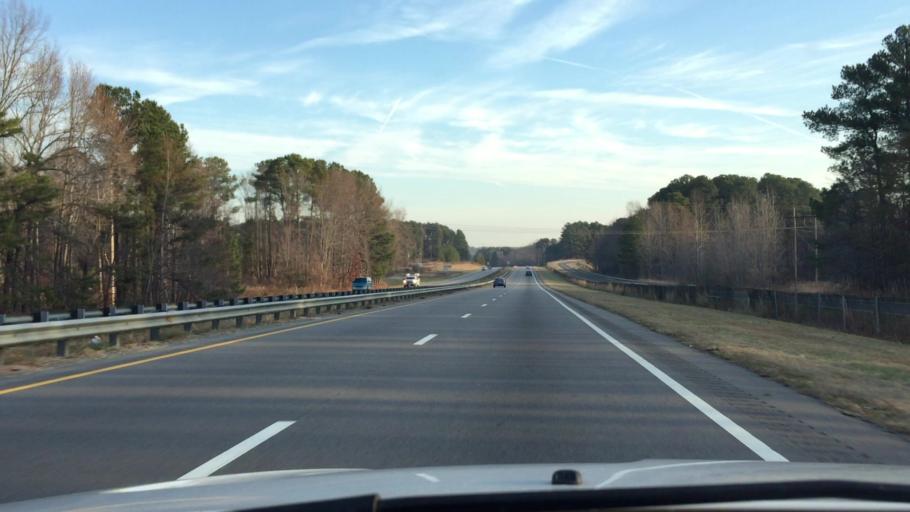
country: US
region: North Carolina
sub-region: Lee County
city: Sanford
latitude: 35.4553
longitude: -79.2111
